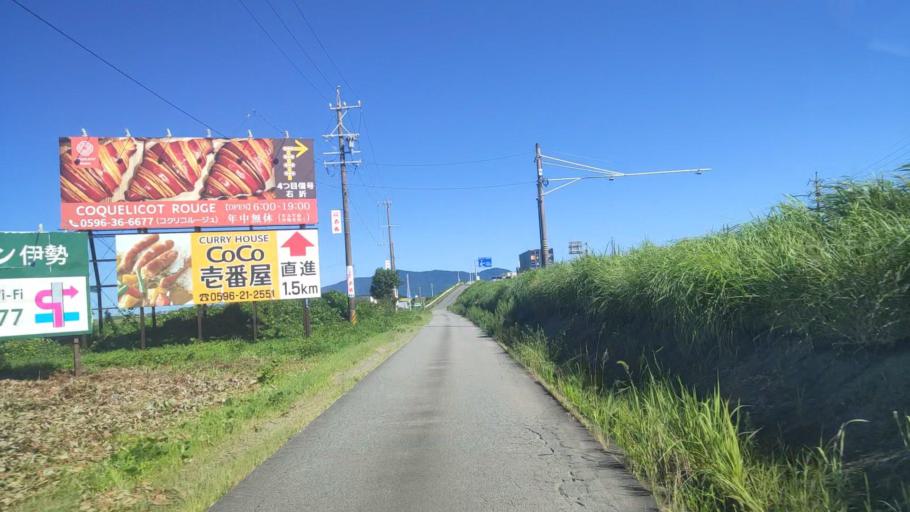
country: JP
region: Mie
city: Ise
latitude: 34.5156
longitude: 136.6915
